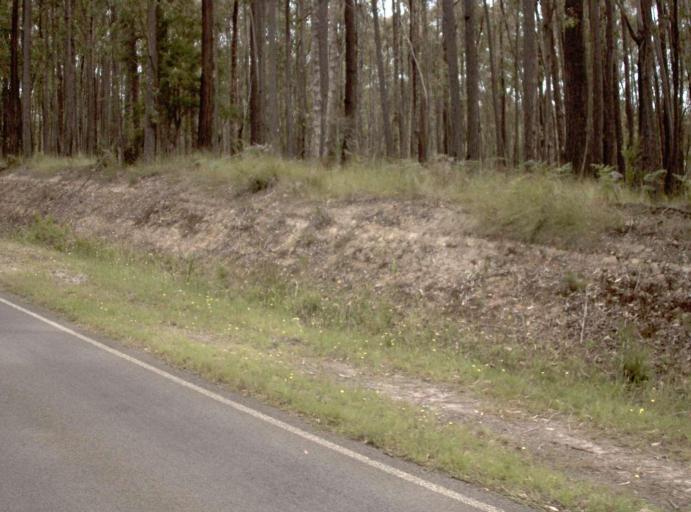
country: AU
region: Victoria
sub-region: Latrobe
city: Morwell
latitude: -38.0797
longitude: 146.4305
